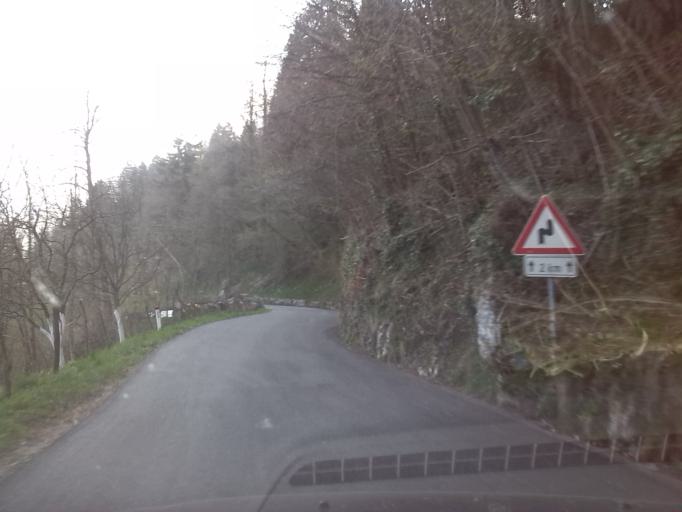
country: IT
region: Friuli Venezia Giulia
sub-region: Provincia di Udine
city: Cras
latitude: 46.2023
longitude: 13.5971
